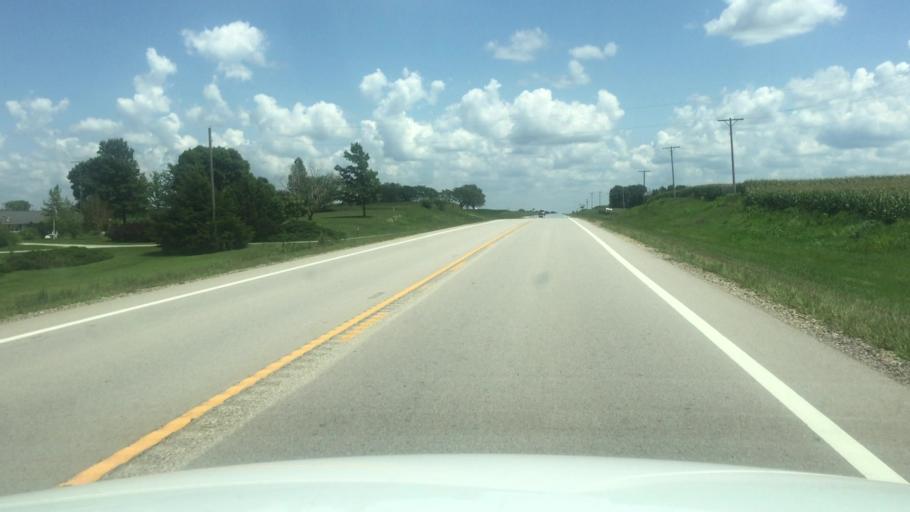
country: US
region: Kansas
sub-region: Brown County
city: Horton
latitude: 39.6672
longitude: -95.4670
